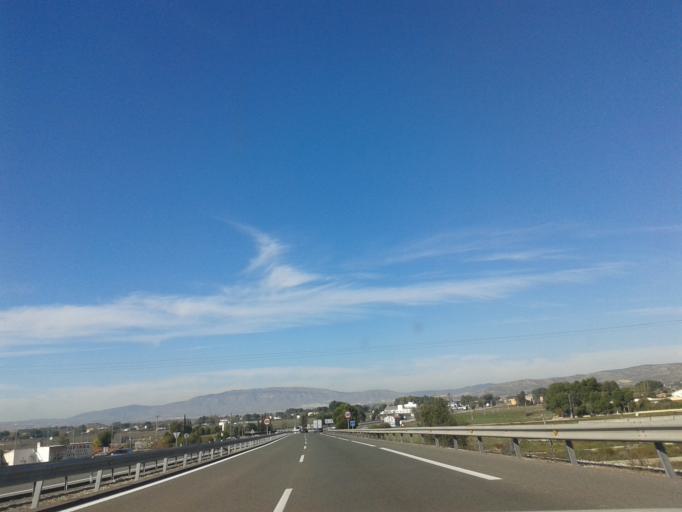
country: ES
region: Valencia
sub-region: Provincia de Alicante
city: Villena
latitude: 38.6480
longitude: -0.8690
